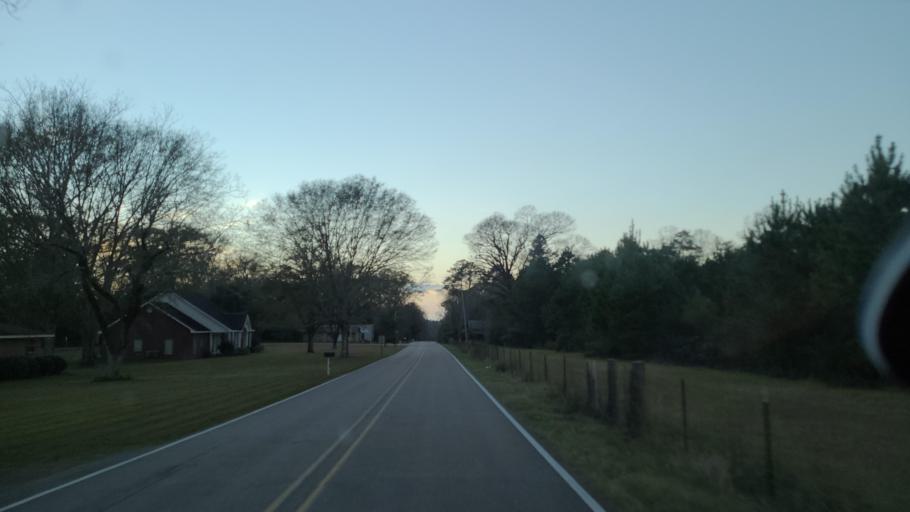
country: US
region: Mississippi
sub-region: Forrest County
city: Hattiesburg
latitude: 31.1677
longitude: -89.2244
